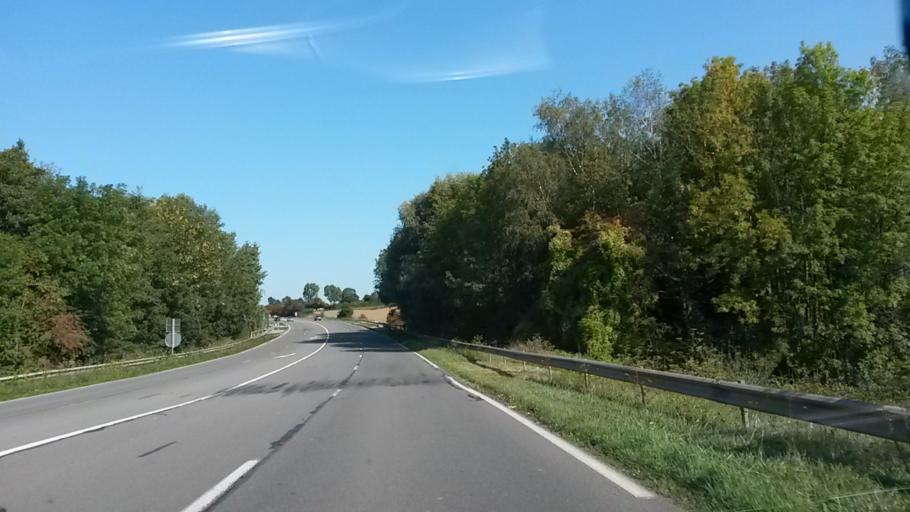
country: FR
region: Nord-Pas-de-Calais
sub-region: Departement du Nord
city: Avesnes-sur-Helpe
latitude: 50.0599
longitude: 3.9332
